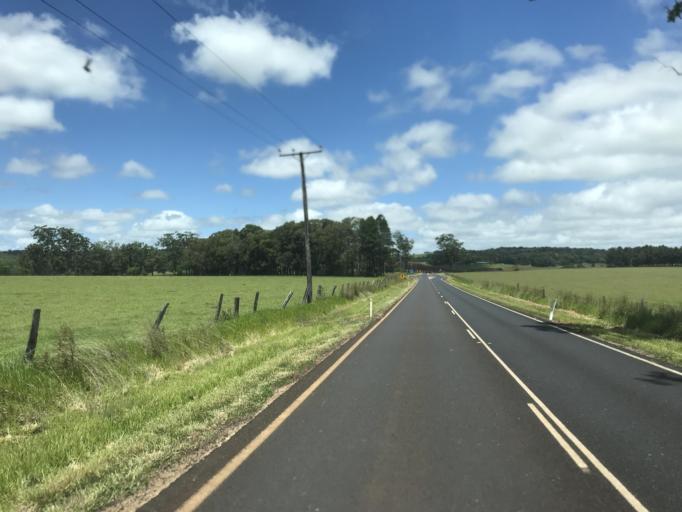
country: AU
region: Queensland
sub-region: Tablelands
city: Ravenshoe
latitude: -17.5108
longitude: 145.4535
